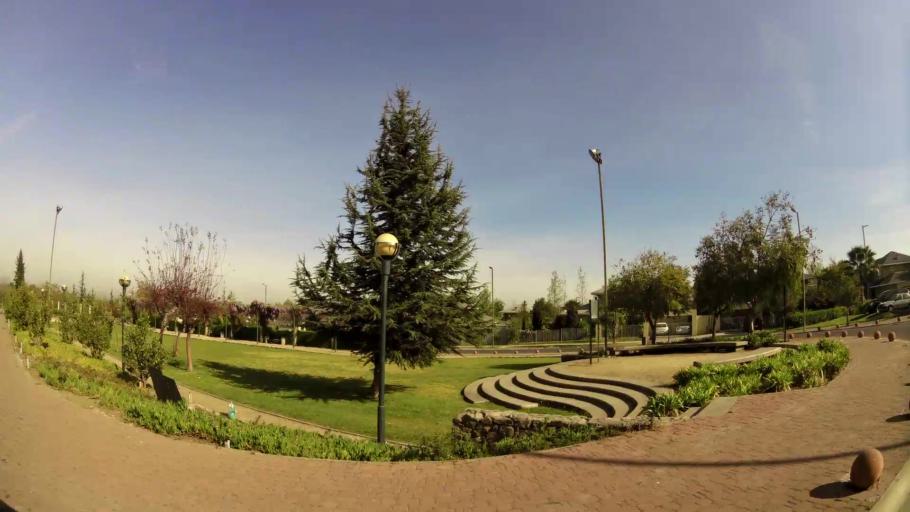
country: CL
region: Santiago Metropolitan
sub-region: Provincia de Santiago
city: Villa Presidente Frei, Nunoa, Santiago, Chile
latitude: -33.4908
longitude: -70.5537
